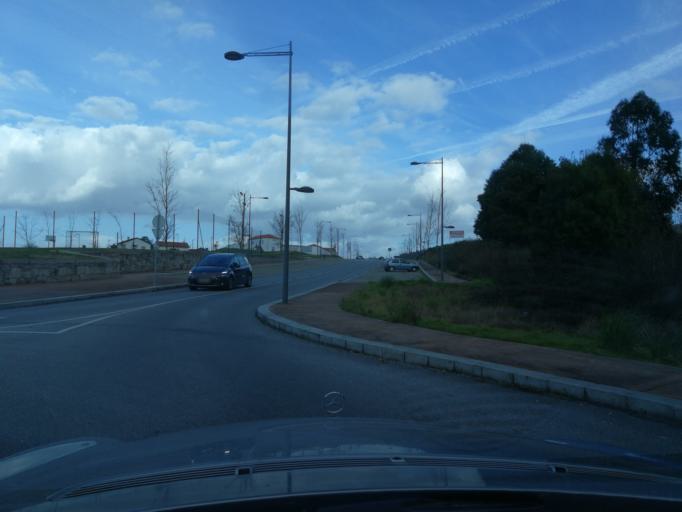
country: PT
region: Viana do Castelo
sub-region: Valenca
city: Valenza
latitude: 42.0303
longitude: -8.6354
